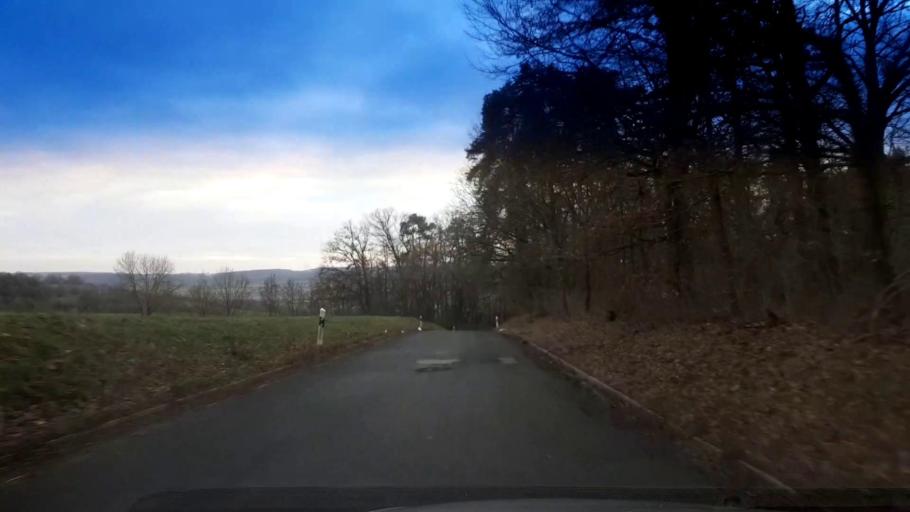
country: DE
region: Bavaria
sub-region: Upper Franconia
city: Lauter
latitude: 49.9560
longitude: 10.7607
